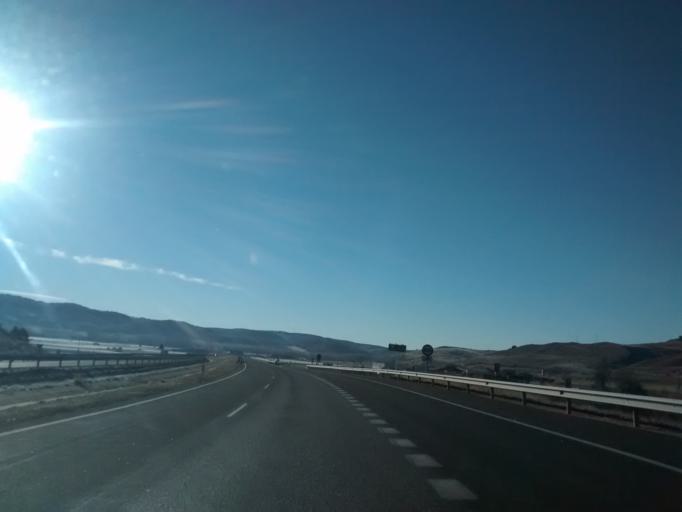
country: ES
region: Castille and Leon
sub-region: Provincia de Palencia
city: Alar del Rey
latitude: 42.7211
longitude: -4.2911
